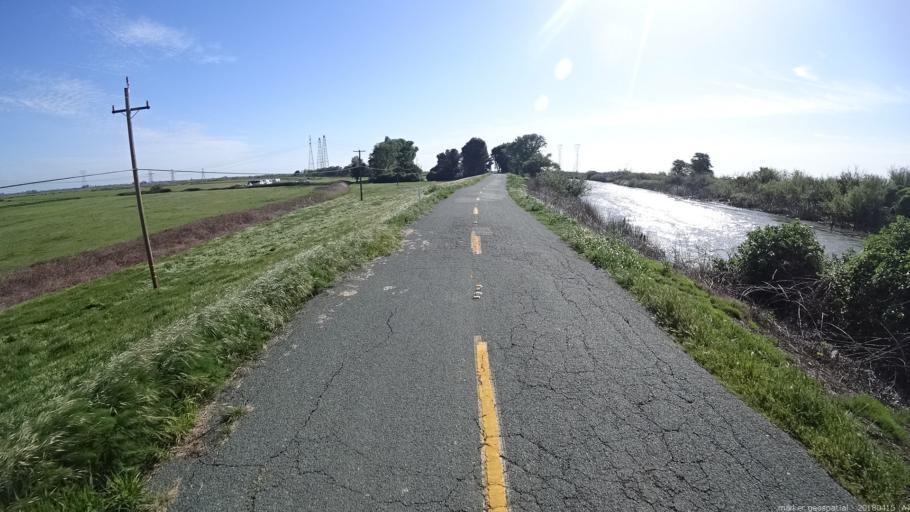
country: US
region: California
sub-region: Contra Costa County
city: Oakley
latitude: 38.0500
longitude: -121.7037
